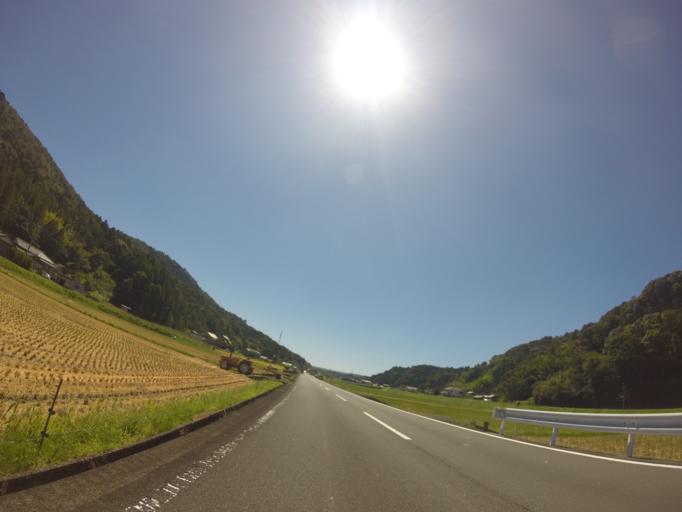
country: JP
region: Shizuoka
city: Kanaya
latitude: 34.8706
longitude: 138.1336
